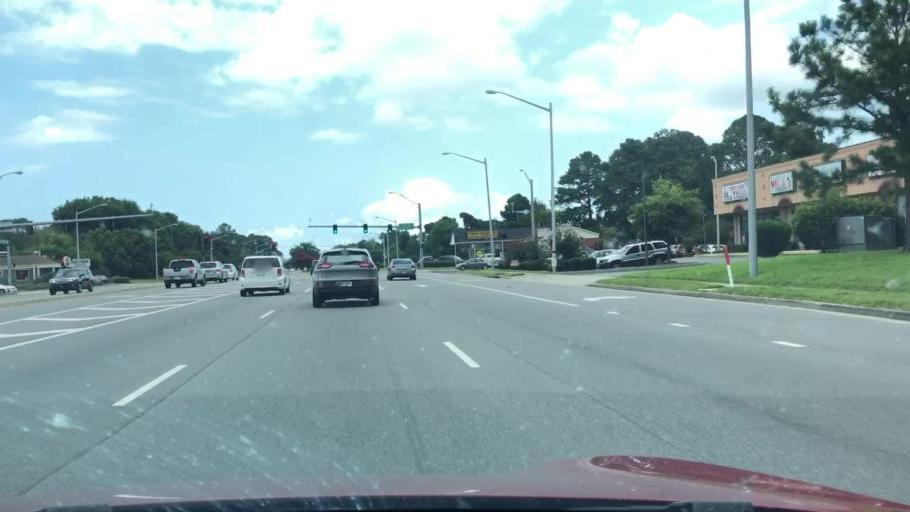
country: US
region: Virginia
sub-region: City of Chesapeake
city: Chesapeake
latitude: 36.8543
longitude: -76.1352
